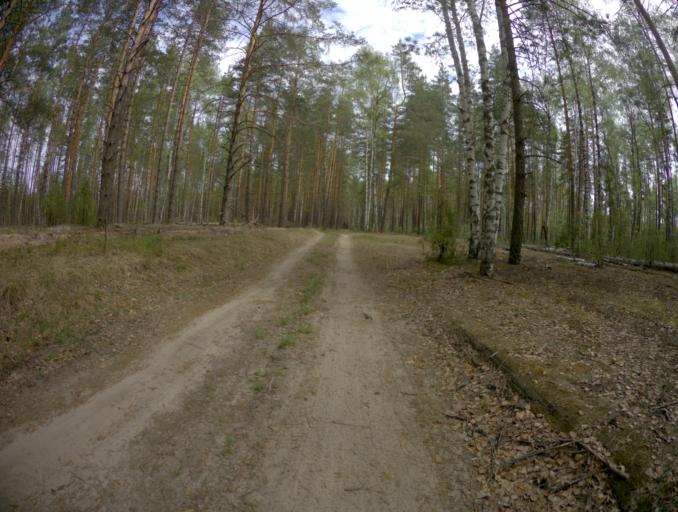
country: RU
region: Ivanovo
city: Yuzha
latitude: 56.4897
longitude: 42.1603
